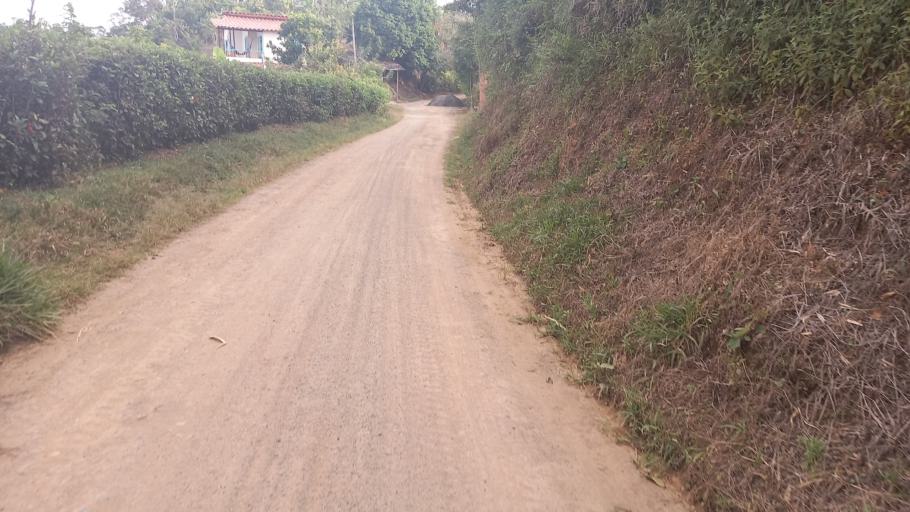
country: CO
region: Antioquia
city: Santa Barbara
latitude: 5.8268
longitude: -75.5758
